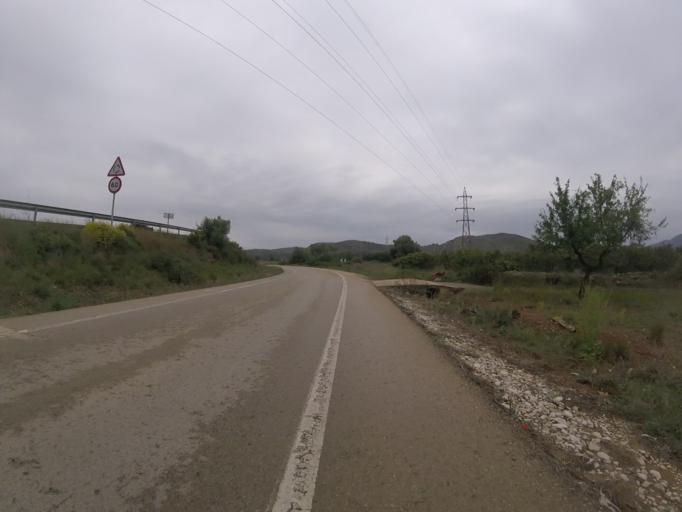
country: ES
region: Valencia
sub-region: Provincia de Castello
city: Alcala de Xivert
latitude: 40.2670
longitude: 0.2416
